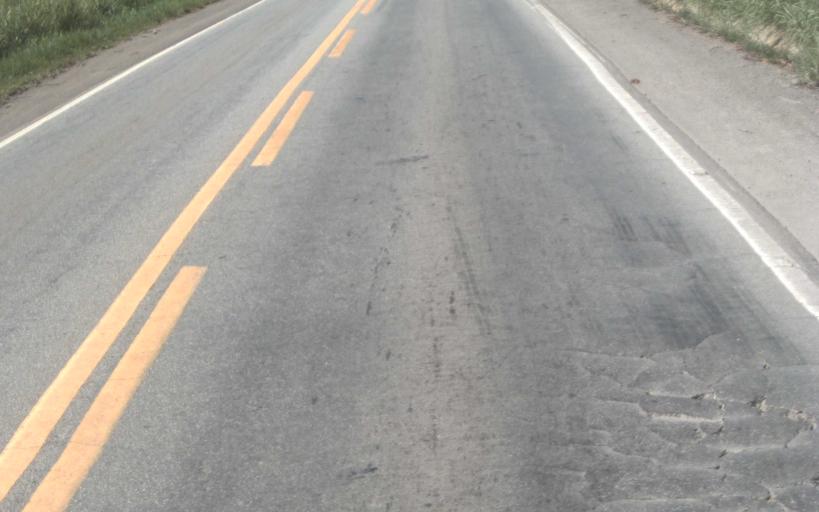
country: BR
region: Minas Gerais
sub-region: Ipaba
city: Ipaba
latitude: -19.3932
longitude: -42.4824
